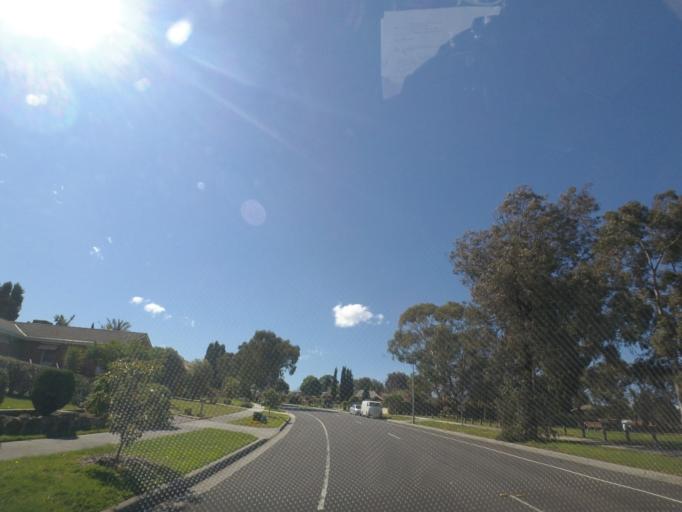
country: AU
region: Victoria
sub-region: Knox
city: Wantirna South
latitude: -37.8698
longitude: 145.2246
